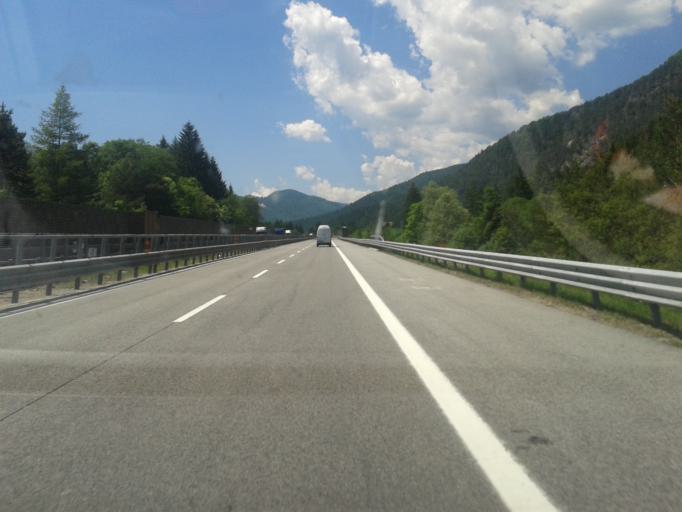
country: IT
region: Friuli Venezia Giulia
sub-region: Provincia di Udine
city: Tarvisio
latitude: 46.5077
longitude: 13.5626
